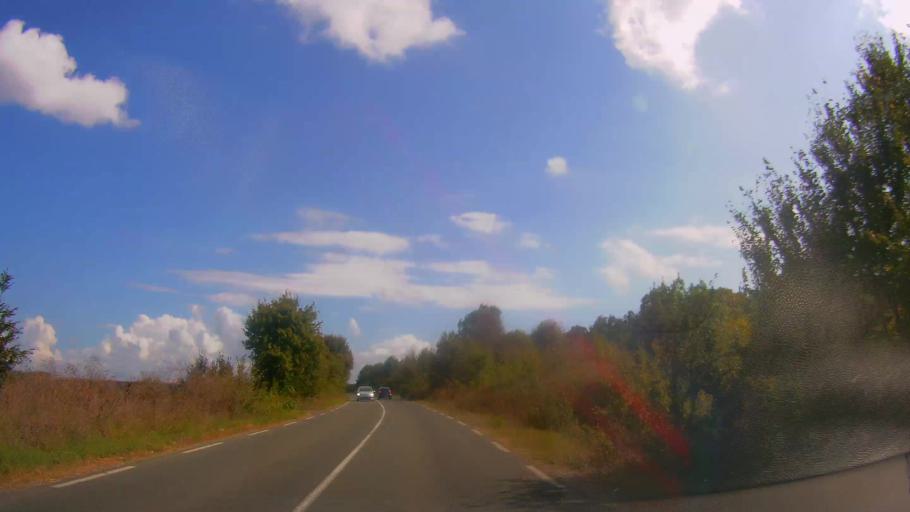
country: BG
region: Burgas
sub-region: Obshtina Kameno
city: Kameno
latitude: 42.4800
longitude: 27.3468
